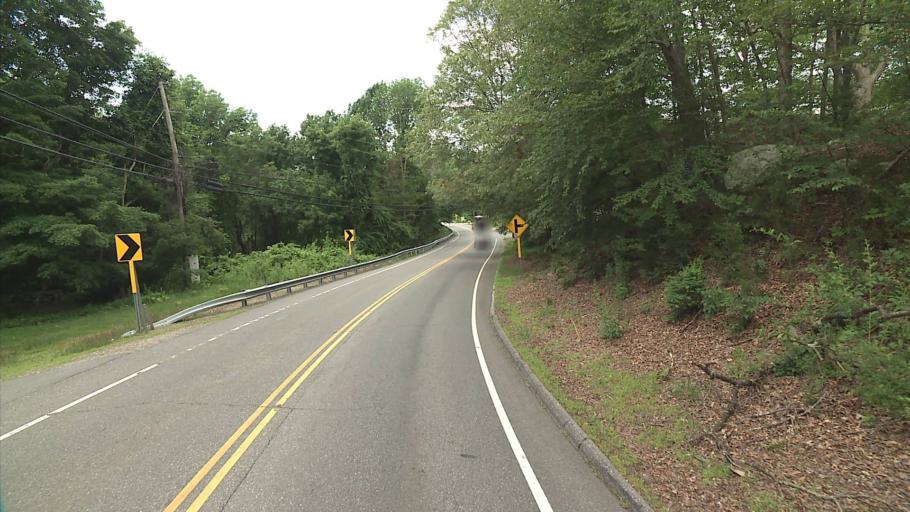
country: US
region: Connecticut
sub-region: New London County
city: Ledyard Center
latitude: 41.4443
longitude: -72.0216
